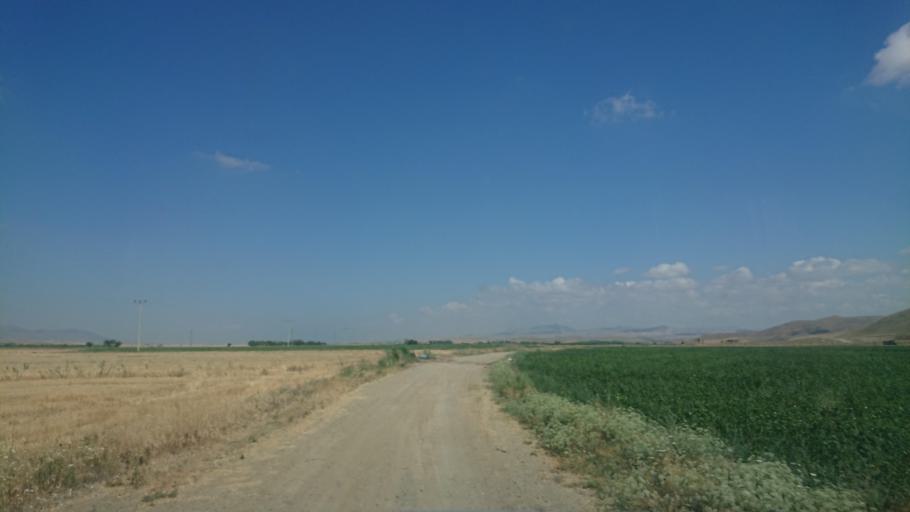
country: TR
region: Aksaray
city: Sariyahsi
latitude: 38.9770
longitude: 33.9115
